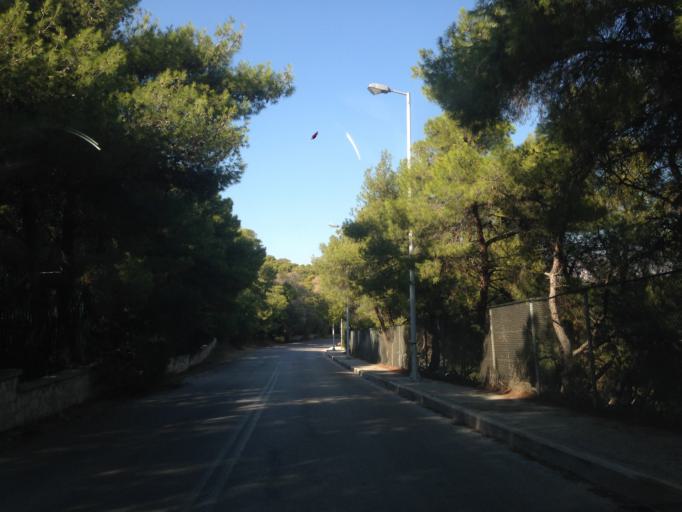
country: GR
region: Attica
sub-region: Nomarchia Anatolikis Attikis
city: Vouliagmeni
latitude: 37.8016
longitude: 23.7715
